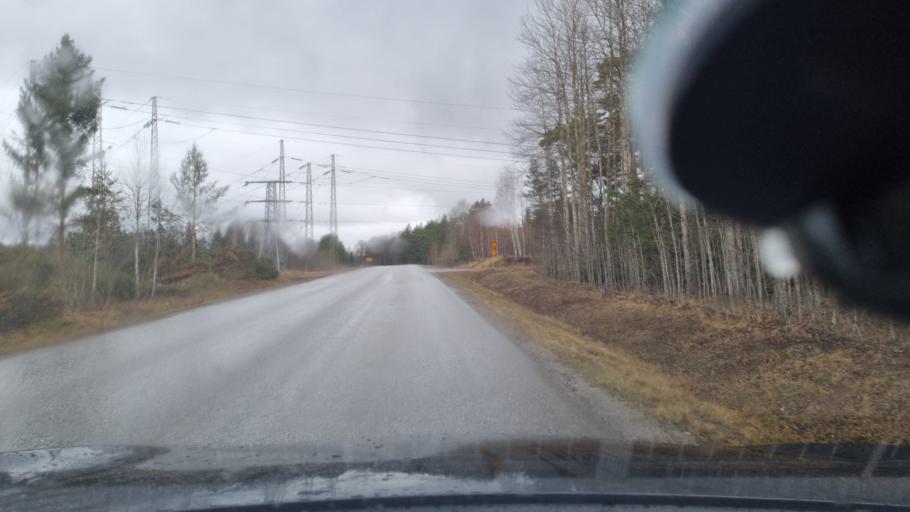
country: SE
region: Stockholm
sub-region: Upplands-Bro Kommun
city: Kungsaengen
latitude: 59.5285
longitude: 17.7505
